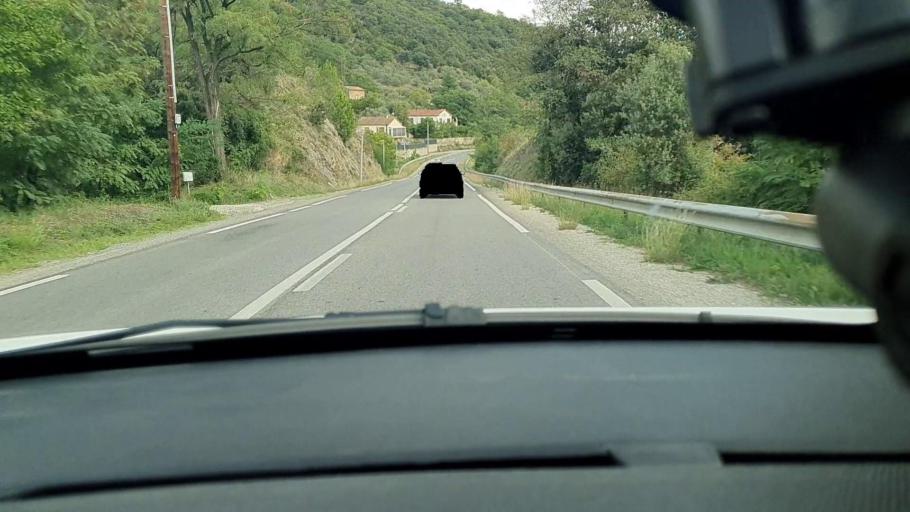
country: FR
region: Languedoc-Roussillon
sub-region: Departement du Gard
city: Les Mages
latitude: 44.2291
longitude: 4.1506
